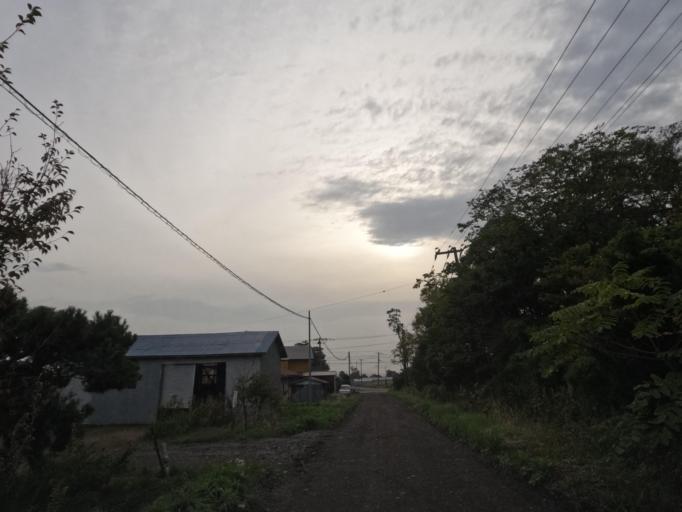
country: JP
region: Hokkaido
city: Date
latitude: 42.4222
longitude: 140.9107
